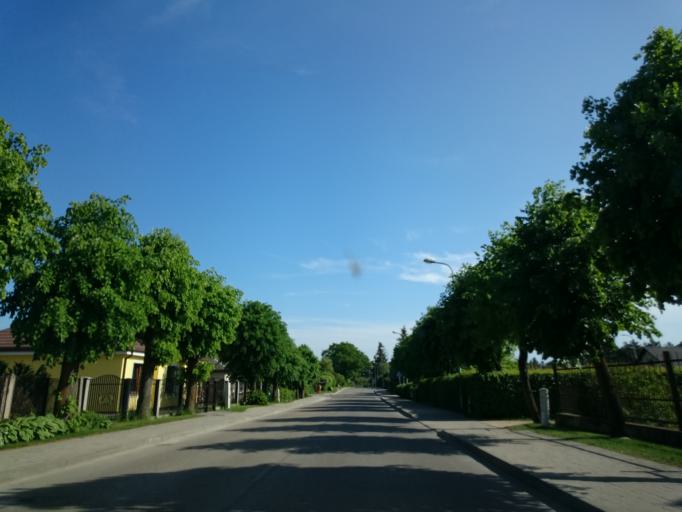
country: LV
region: Dobeles Rajons
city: Dobele
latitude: 56.6134
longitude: 23.2840
